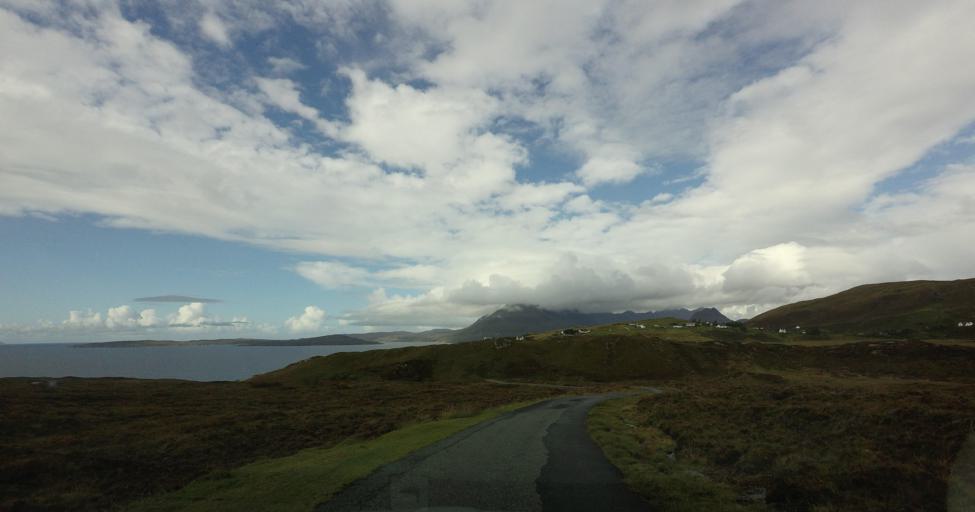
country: GB
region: Scotland
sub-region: Highland
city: Isle of Skye
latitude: 57.1452
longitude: -6.0918
